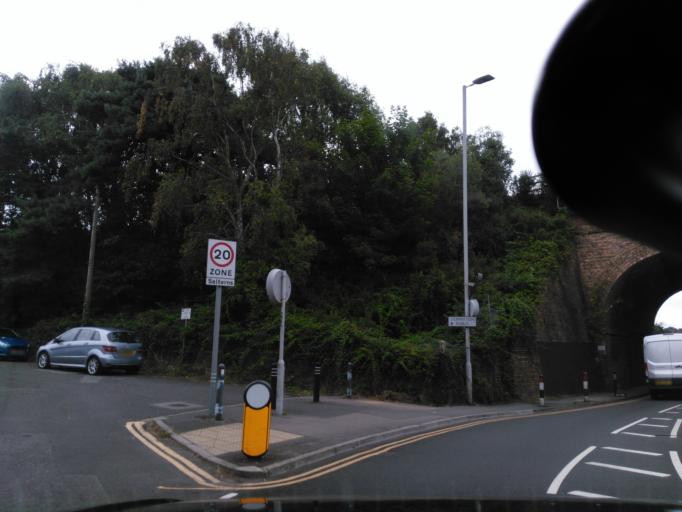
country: GB
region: England
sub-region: Dorset
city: Parkstone
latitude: 50.7206
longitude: -1.9551
